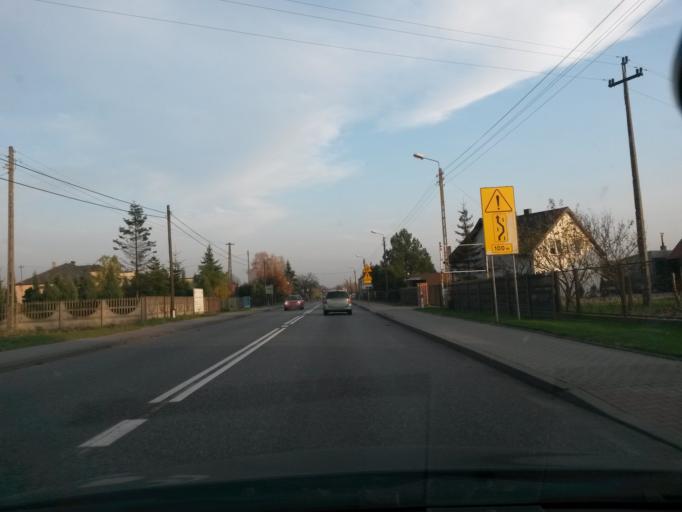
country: PL
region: Lodz Voivodeship
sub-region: Powiat wielunski
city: Wielun
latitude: 51.2291
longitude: 18.5488
